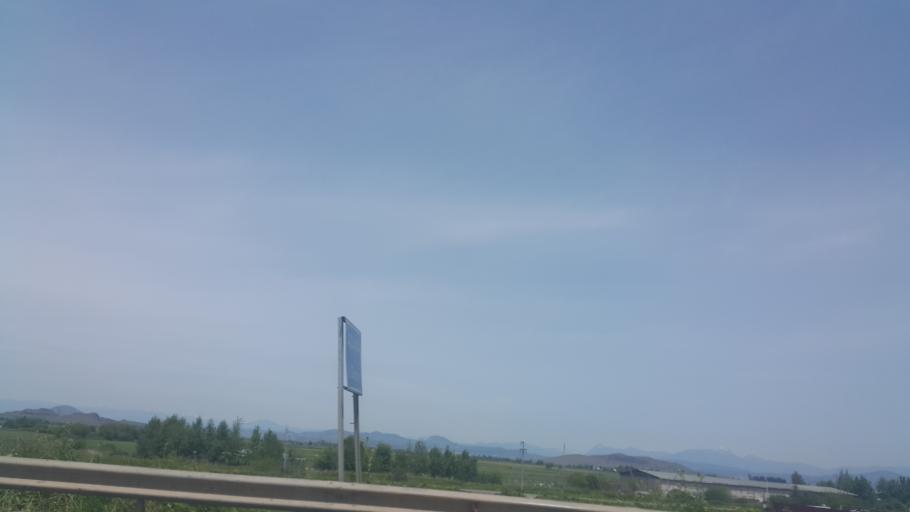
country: TR
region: Osmaniye
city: Toprakkale
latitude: 37.0736
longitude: 36.0858
